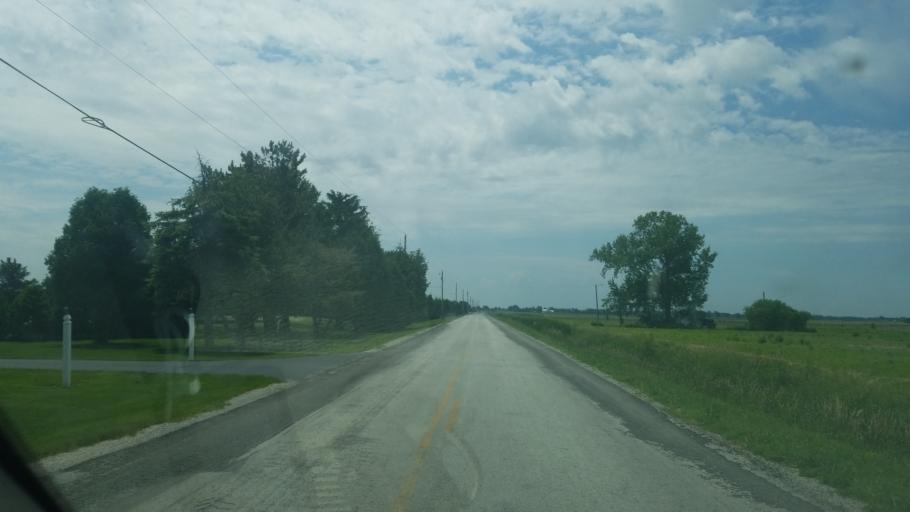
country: US
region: Ohio
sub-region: Wood County
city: Bowling Green
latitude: 41.2890
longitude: -83.5926
